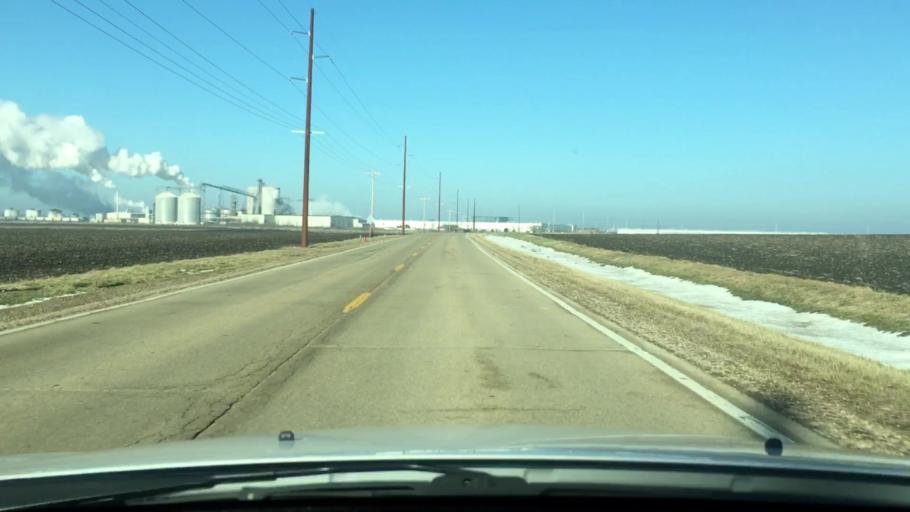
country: US
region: Illinois
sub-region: Ogle County
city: Rochelle
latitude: 41.8852
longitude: -89.0259
